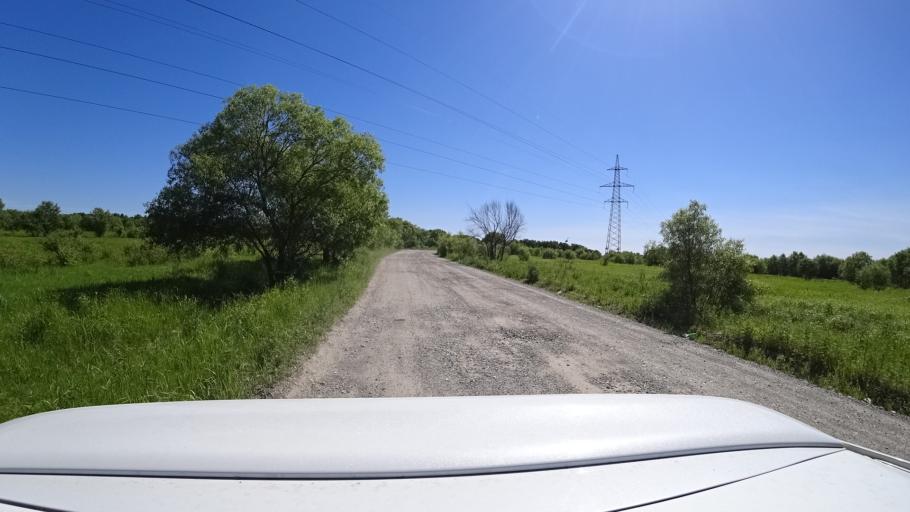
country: RU
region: Khabarovsk Krai
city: Topolevo
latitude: 48.5633
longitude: 135.1967
